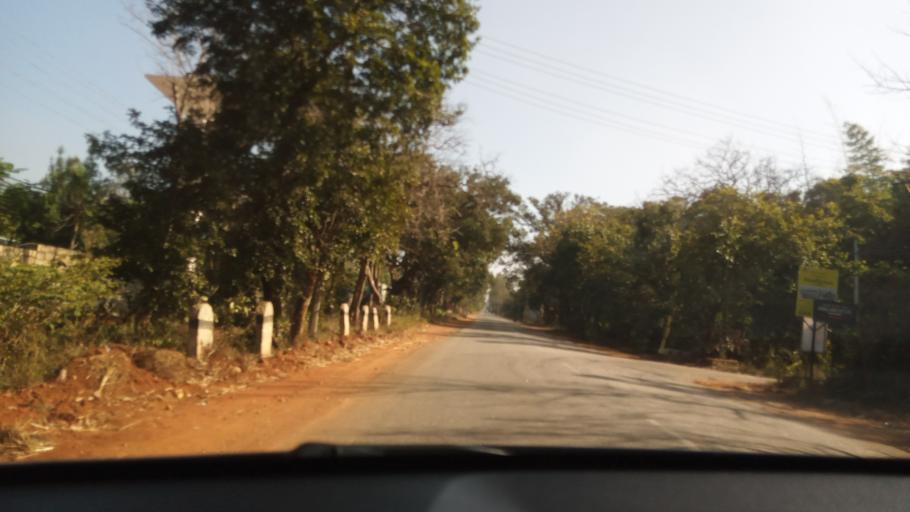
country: IN
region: Karnataka
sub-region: Bangalore Rural
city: Devanhalli
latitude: 13.2662
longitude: 77.7405
